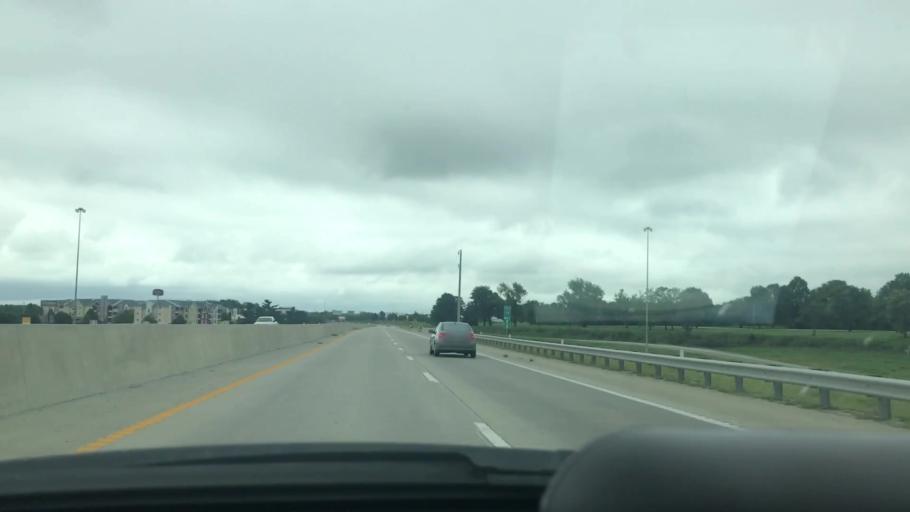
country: US
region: Missouri
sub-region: Jasper County
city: Duquesne
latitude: 37.0464
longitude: -94.4799
